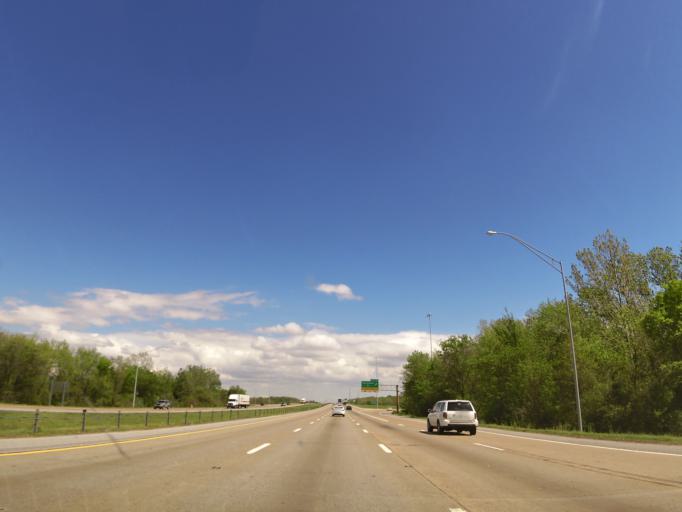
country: US
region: Tennessee
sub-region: Shelby County
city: Memphis
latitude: 35.1921
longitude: -89.9833
